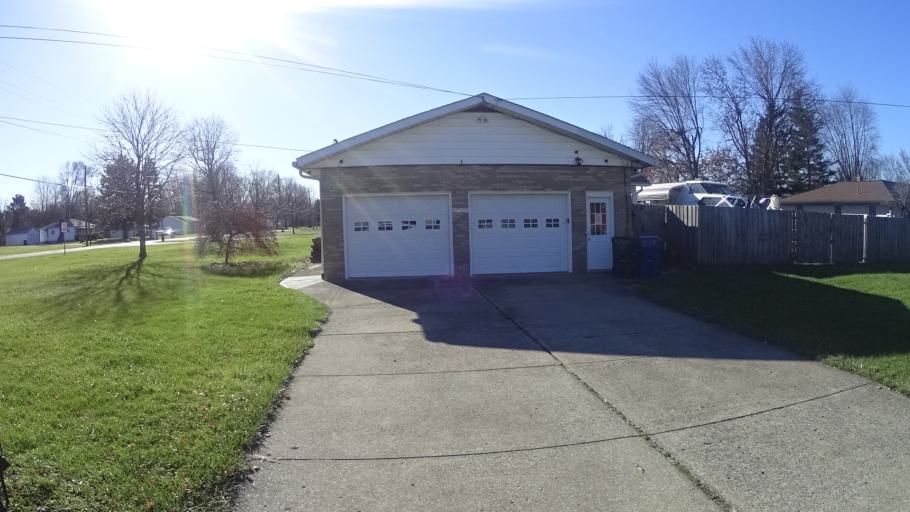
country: US
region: Ohio
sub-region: Lorain County
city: Elyria
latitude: 41.3956
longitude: -82.1503
